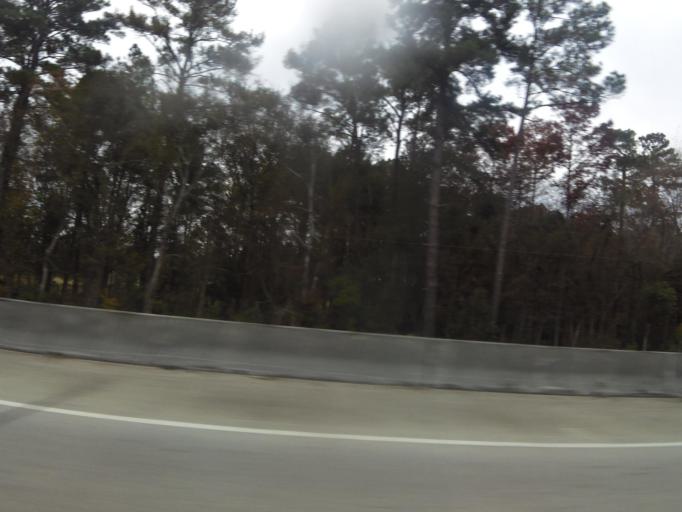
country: US
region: Georgia
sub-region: Charlton County
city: Folkston
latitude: 30.9080
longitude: -82.0719
